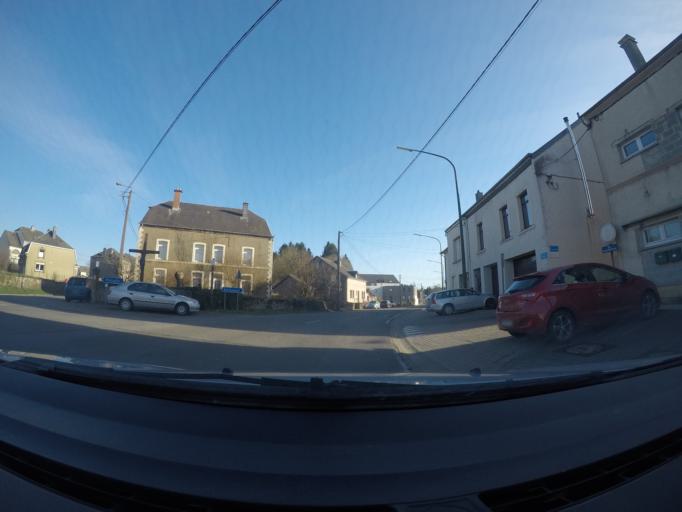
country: BE
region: Wallonia
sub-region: Province du Luxembourg
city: Tintigny
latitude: 49.6824
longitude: 5.5135
